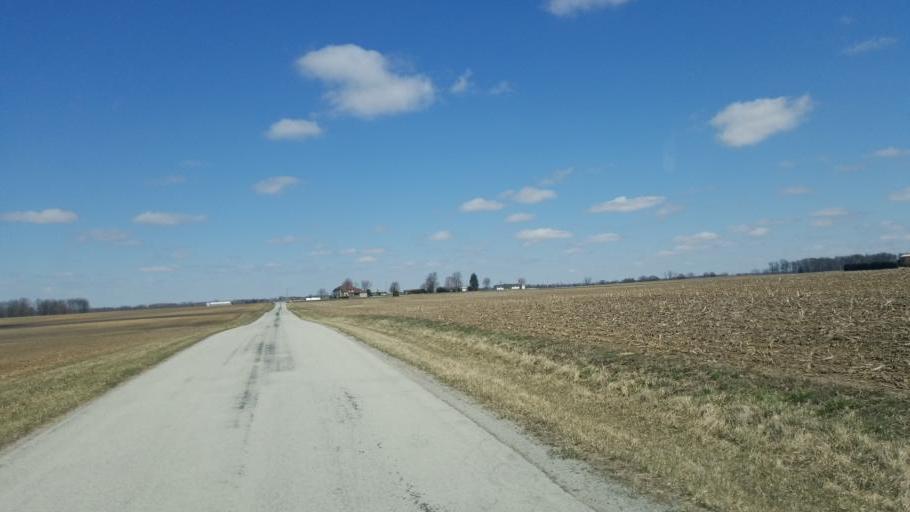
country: US
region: Ohio
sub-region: Wyandot County
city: Upper Sandusky
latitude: 40.7355
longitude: -83.1883
